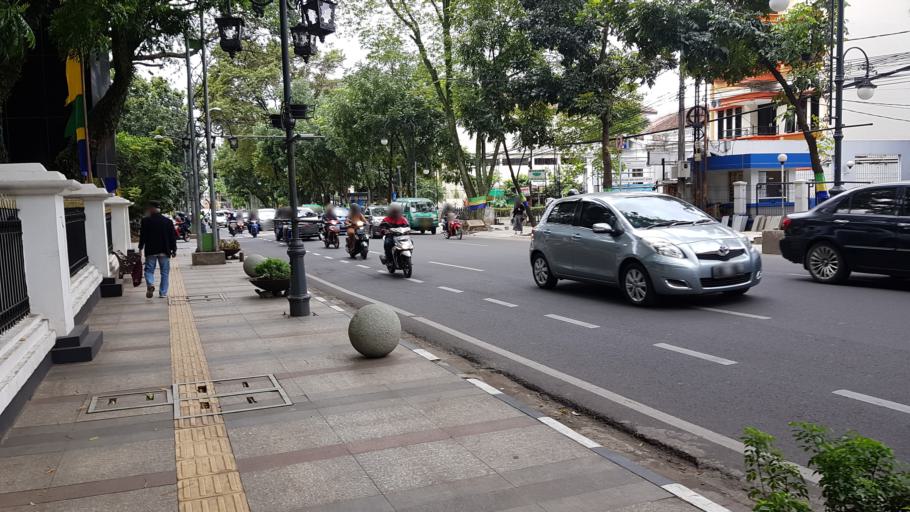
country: ID
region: West Java
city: Bandung
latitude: -6.9123
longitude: 107.6091
